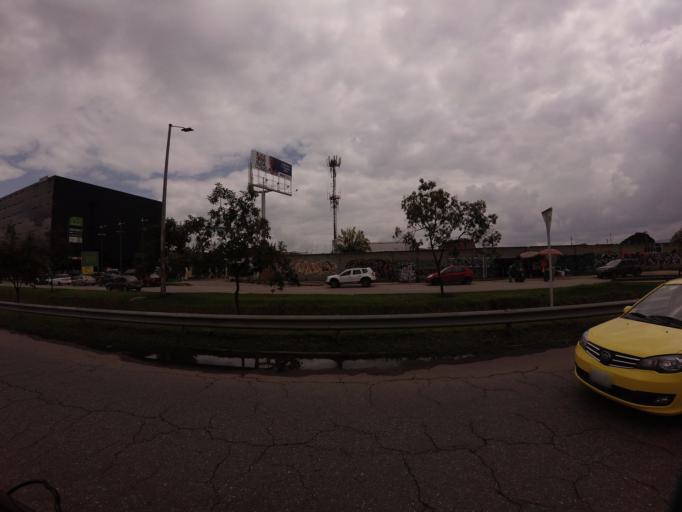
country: CO
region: Bogota D.C.
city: Bogota
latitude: 4.6865
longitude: -74.1264
